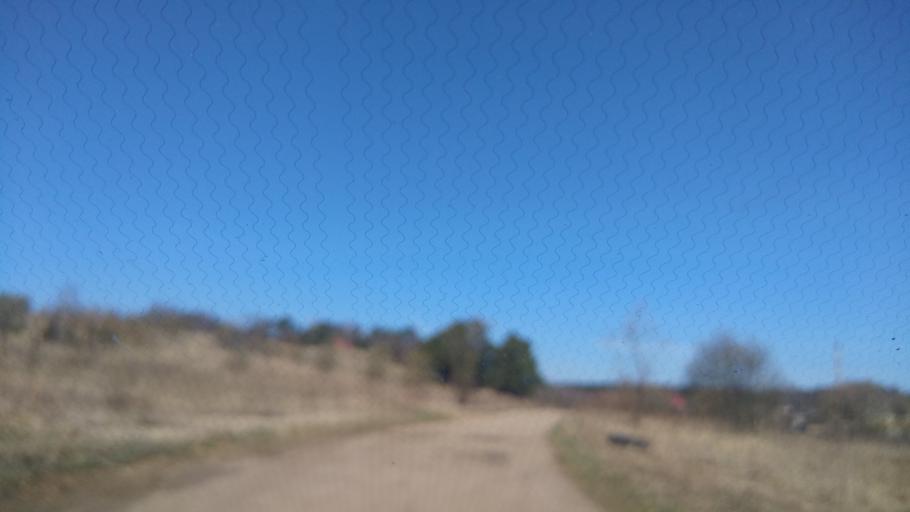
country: RU
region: Moskovskaya
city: Khot'kovo
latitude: 56.1888
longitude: 38.0317
